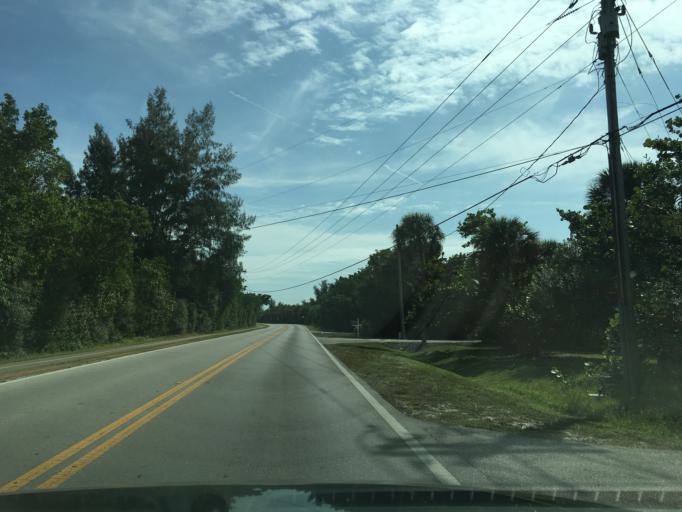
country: US
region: Florida
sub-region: Lee County
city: Saint James City
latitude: 26.4770
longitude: -82.1755
